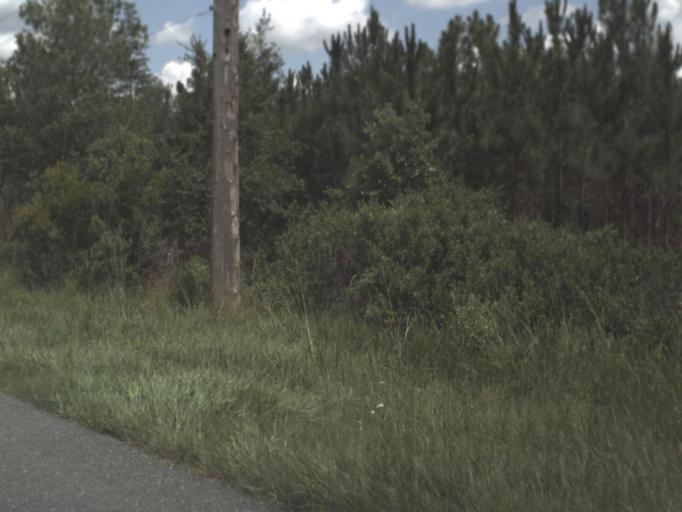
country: US
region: Florida
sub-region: Gilchrist County
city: Trenton
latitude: 29.6194
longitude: -82.7722
